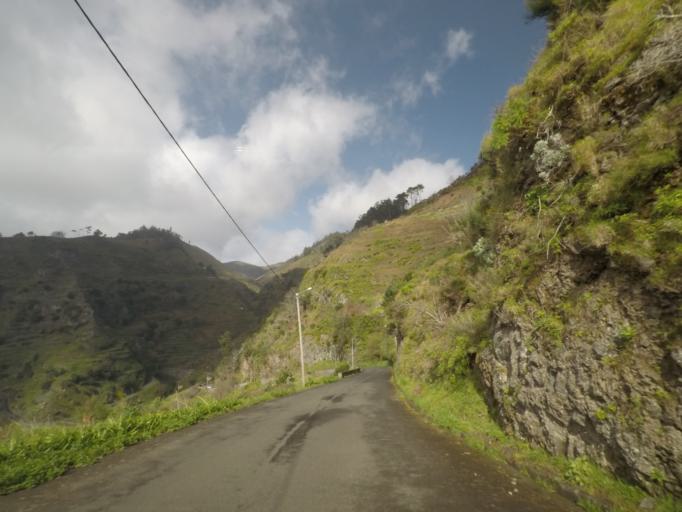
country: PT
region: Madeira
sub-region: Ribeira Brava
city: Campanario
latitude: 32.6997
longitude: -17.0262
